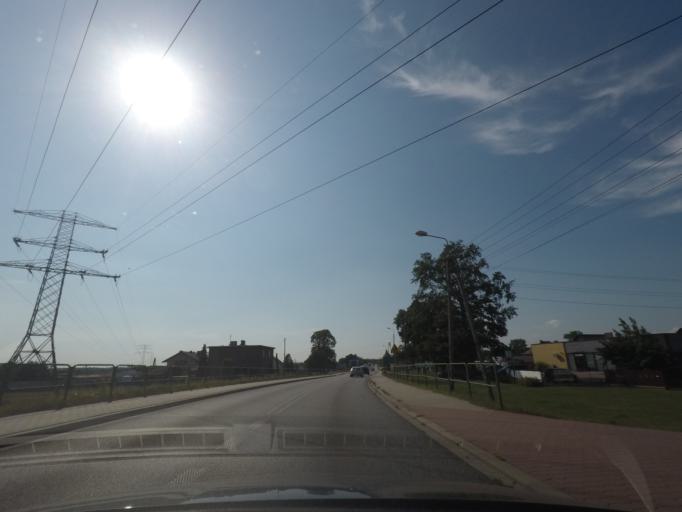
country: PL
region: Silesian Voivodeship
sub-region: Powiat pszczynski
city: Rudziczka
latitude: 50.0363
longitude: 18.7571
